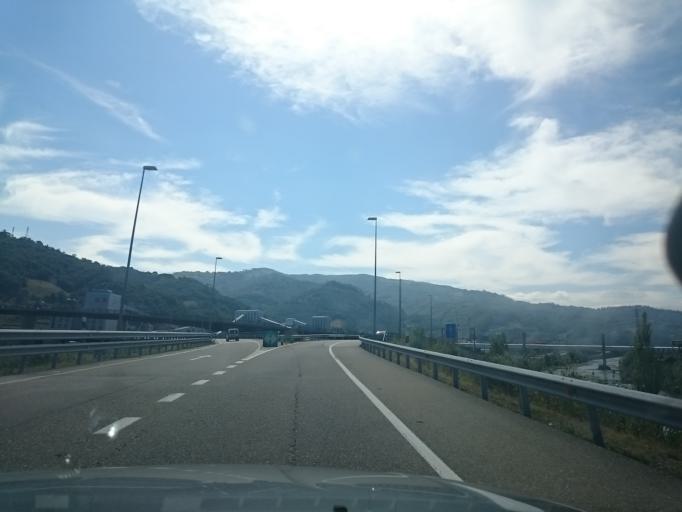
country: ES
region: Asturias
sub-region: Province of Asturias
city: Mieres
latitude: 43.2624
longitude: -5.7850
